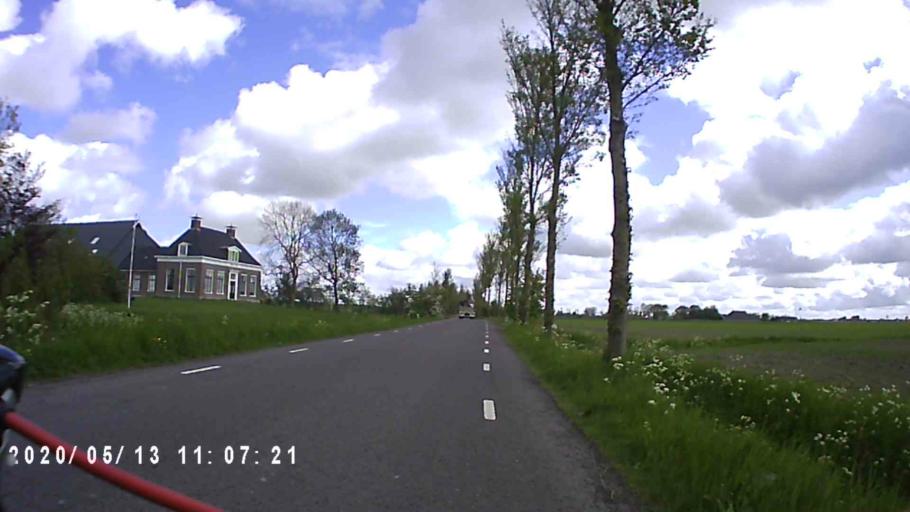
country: NL
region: Groningen
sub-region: Gemeente Zuidhorn
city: Grijpskerk
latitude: 53.2908
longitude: 6.3342
